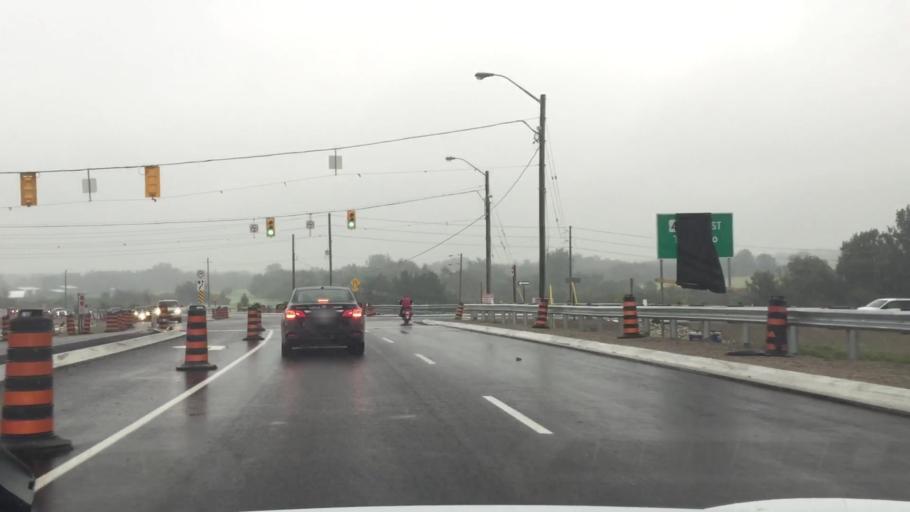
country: CA
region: Ontario
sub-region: Oxford County
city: Woodstock
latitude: 43.1093
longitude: -80.7359
